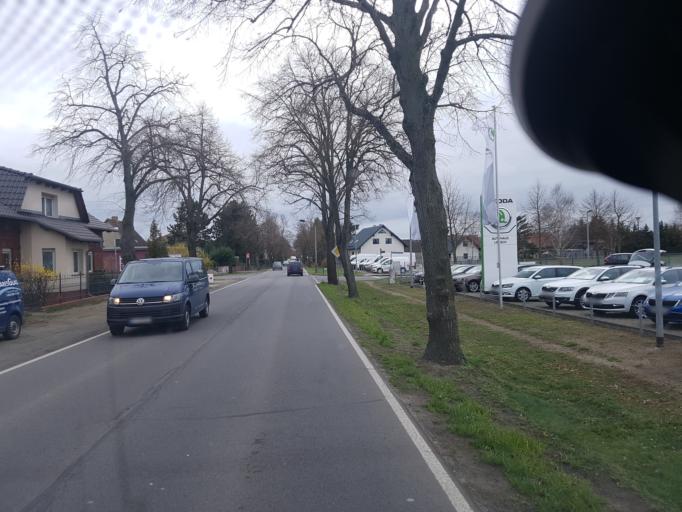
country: DE
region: Brandenburg
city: Luebben
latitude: 51.9485
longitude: 13.9185
